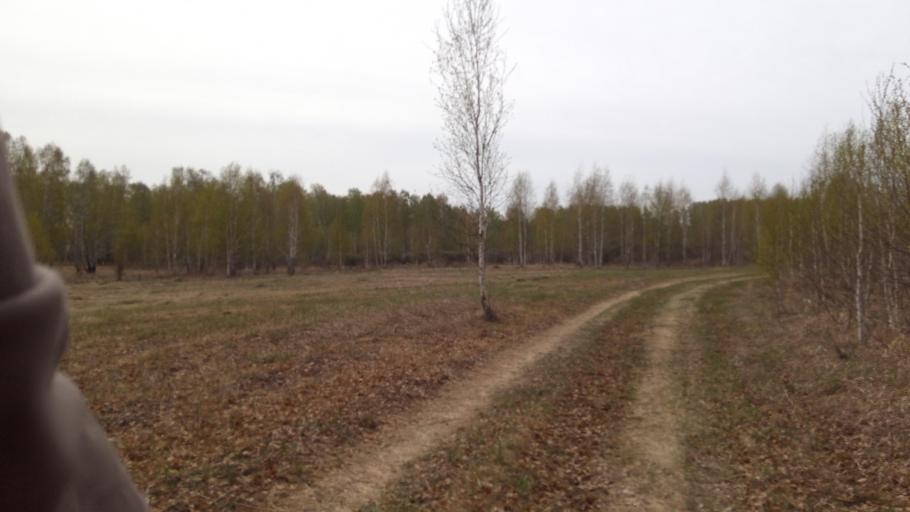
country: RU
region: Chelyabinsk
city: Timiryazevskiy
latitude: 55.0077
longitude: 60.8588
